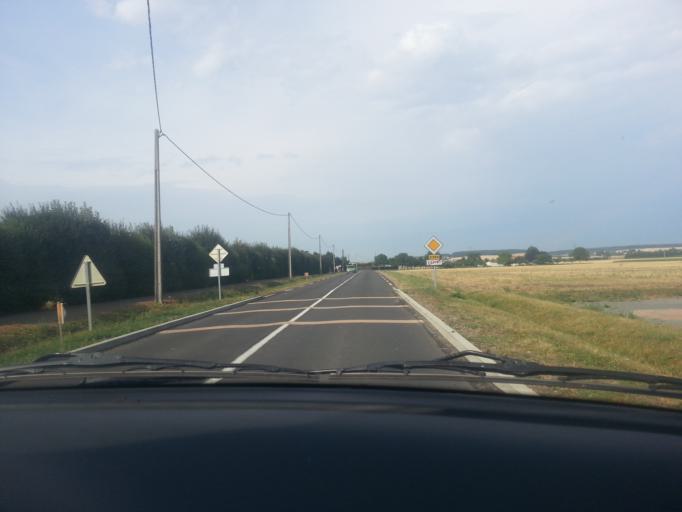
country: FR
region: Auvergne
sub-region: Departement du Puy-de-Dome
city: Aigueperse
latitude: 46.0440
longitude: 3.2575
